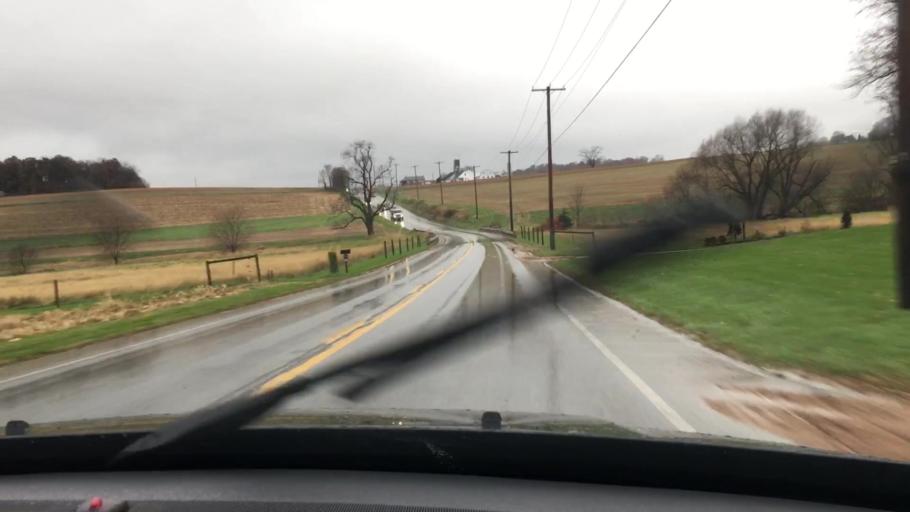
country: US
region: Pennsylvania
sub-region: Lancaster County
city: Quarryville
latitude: 39.8717
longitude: -76.2385
